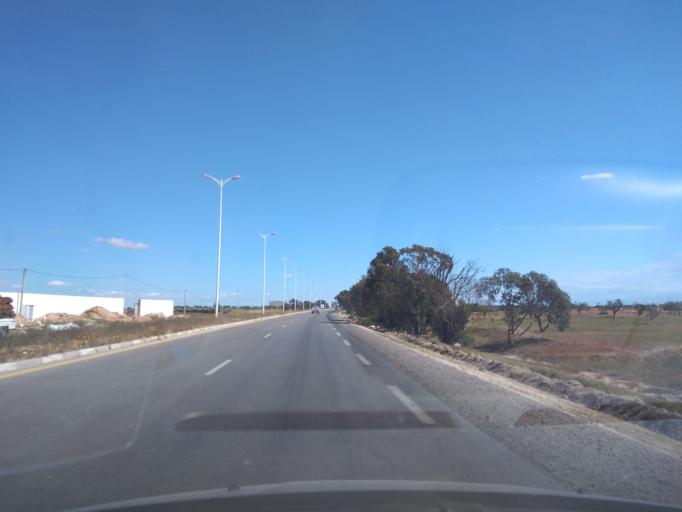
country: TN
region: Safaqis
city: Al Qarmadah
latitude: 34.8405
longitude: 10.7379
